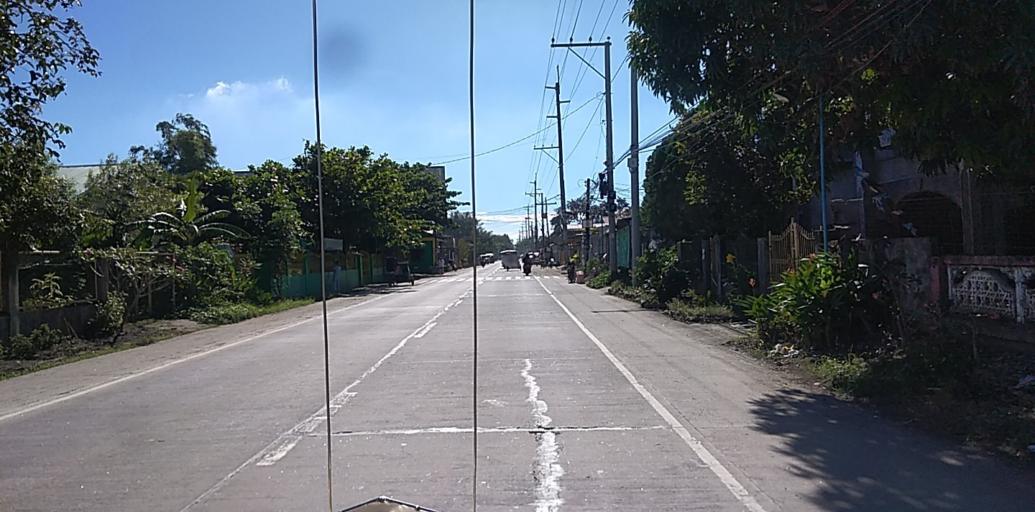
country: PH
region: Central Luzon
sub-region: Province of Pampanga
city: Santo Domingo
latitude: 15.0599
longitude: 120.7734
